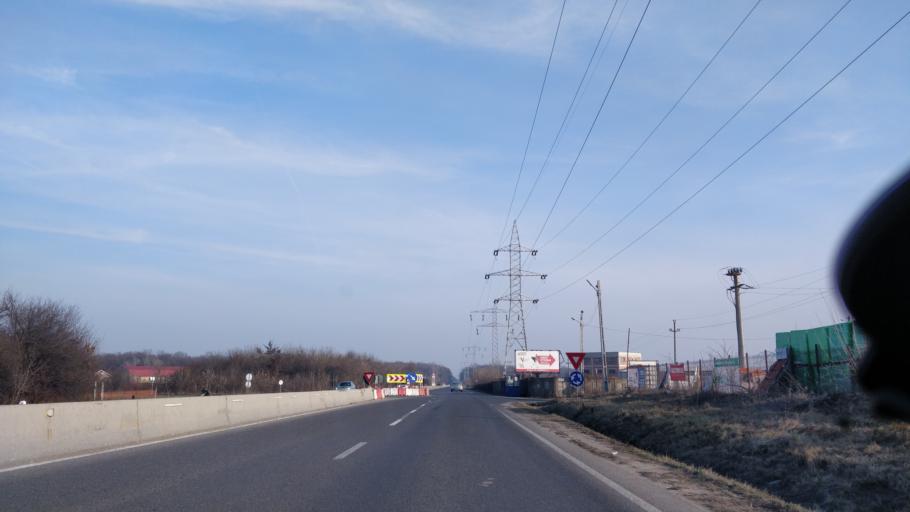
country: RO
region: Dambovita
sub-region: Comuna Tartasesti
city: Gulia
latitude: 44.5536
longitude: 25.8732
